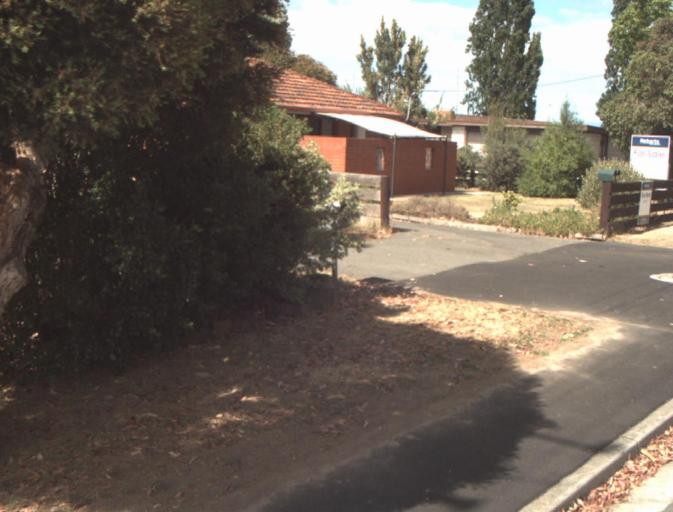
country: AU
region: Tasmania
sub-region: Launceston
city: Summerhill
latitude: -41.4641
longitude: 147.1362
